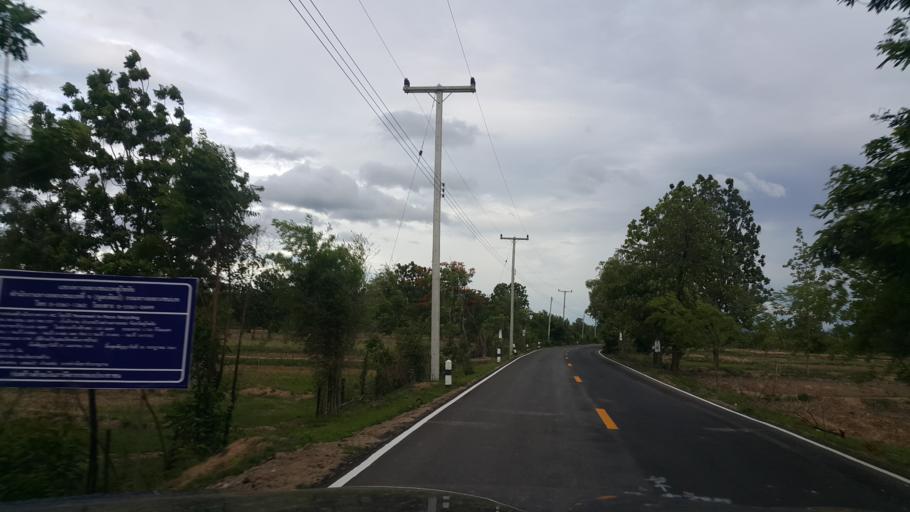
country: TH
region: Sukhothai
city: Thung Saliam
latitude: 17.1731
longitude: 99.4854
